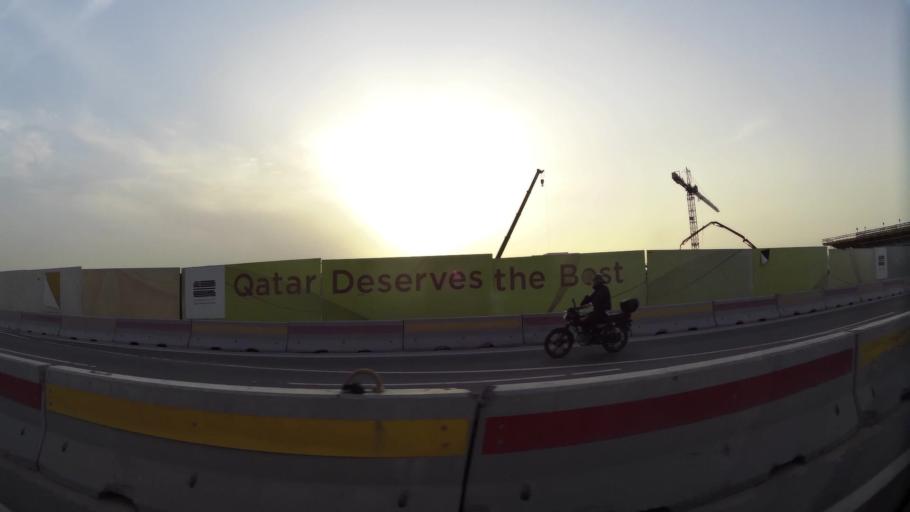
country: QA
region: Baladiyat ad Dawhah
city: Doha
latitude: 25.3515
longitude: 51.5210
